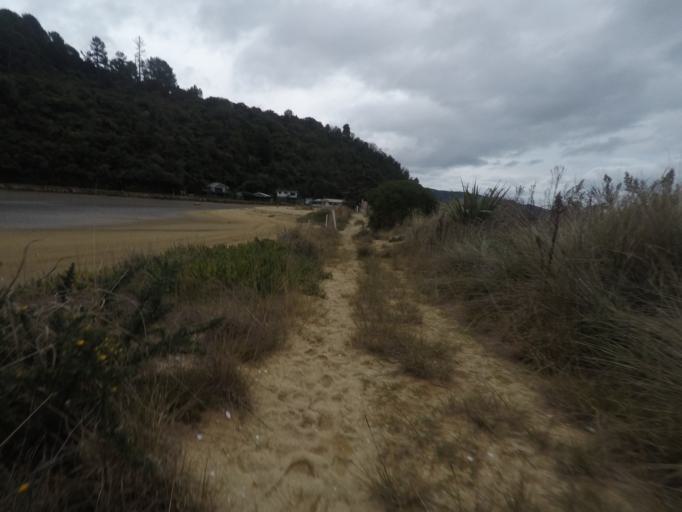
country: NZ
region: Tasman
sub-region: Tasman District
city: Motueka
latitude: -41.0103
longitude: 173.0073
